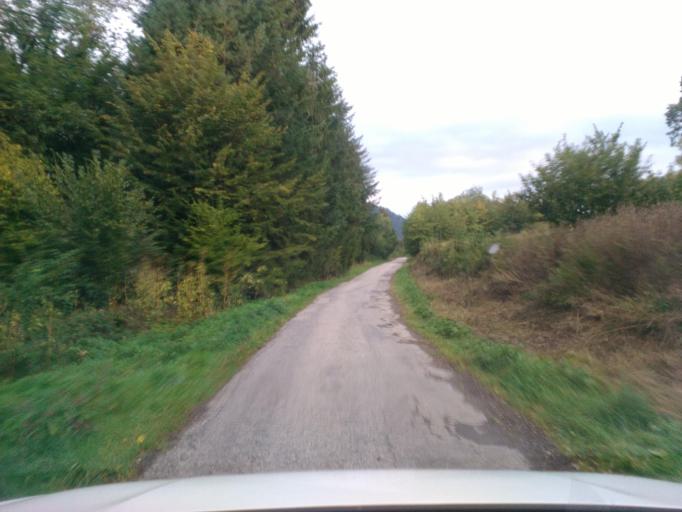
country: FR
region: Lorraine
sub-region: Departement des Vosges
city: Senones
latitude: 48.3942
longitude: 7.0377
